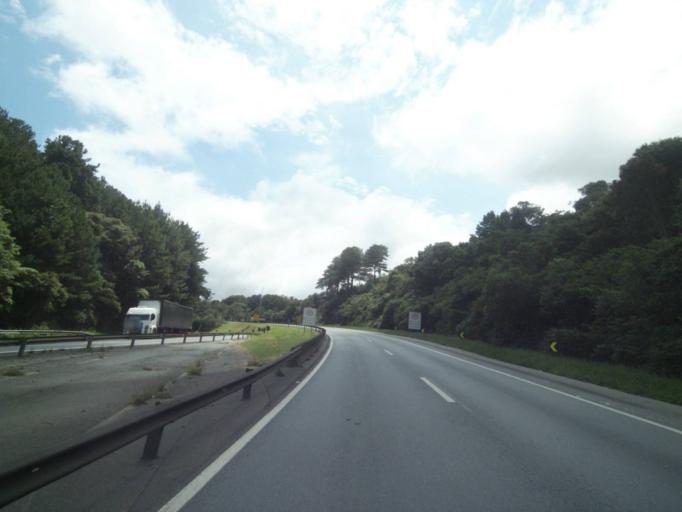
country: BR
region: Parana
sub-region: Campina Grande Do Sul
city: Campina Grande do Sul
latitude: -25.1919
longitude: -48.8859
